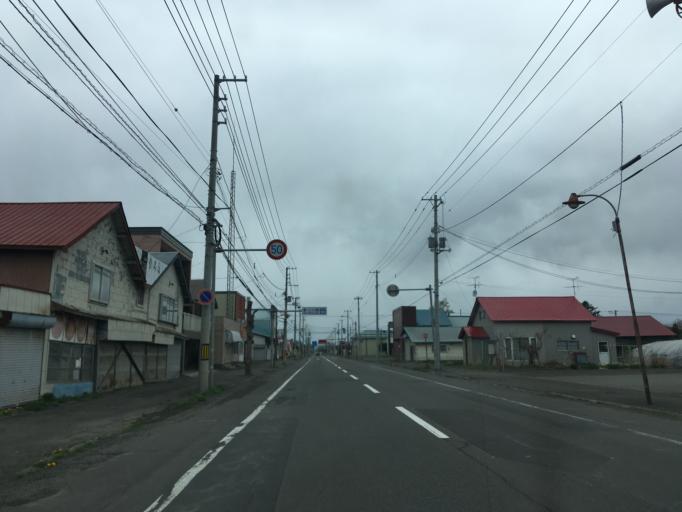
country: JP
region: Hokkaido
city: Chitose
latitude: 42.9442
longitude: 141.8039
